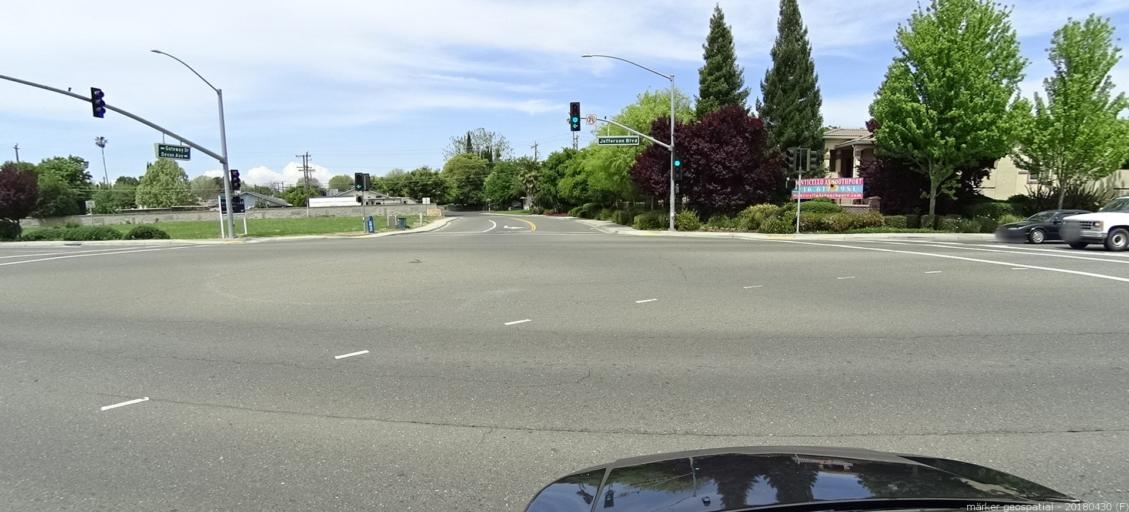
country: US
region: California
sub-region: Yolo County
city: West Sacramento
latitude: 38.5564
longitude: -121.5330
